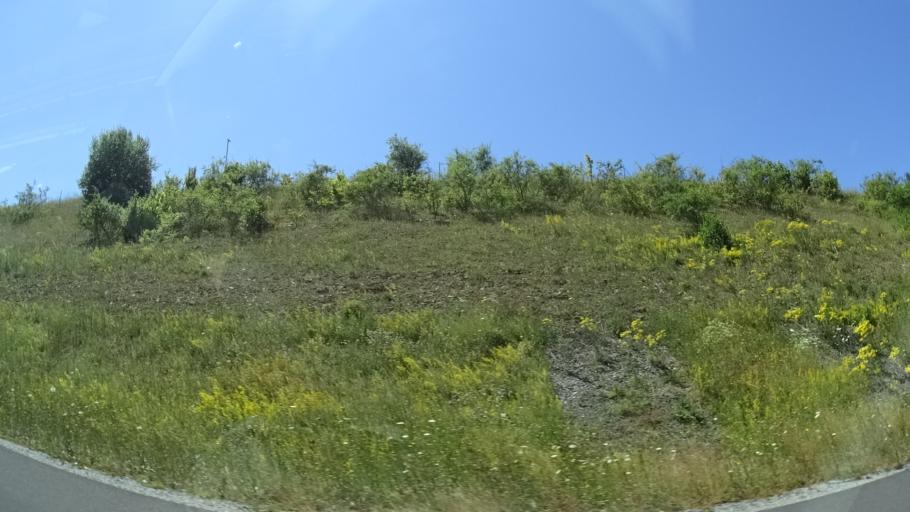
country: DE
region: Bavaria
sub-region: Regierungsbezirk Unterfranken
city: Poppenhausen
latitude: 50.1183
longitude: 10.1557
